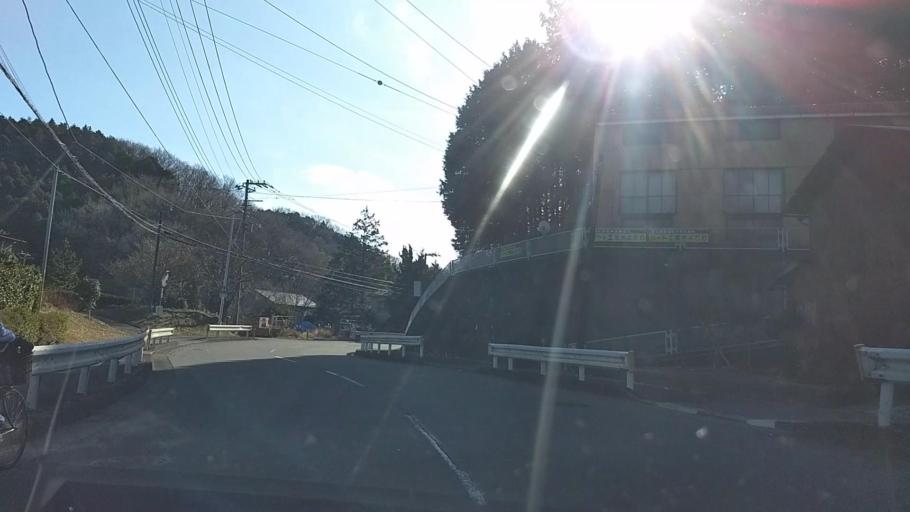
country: JP
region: Kanagawa
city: Atsugi
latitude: 35.4694
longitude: 139.2877
